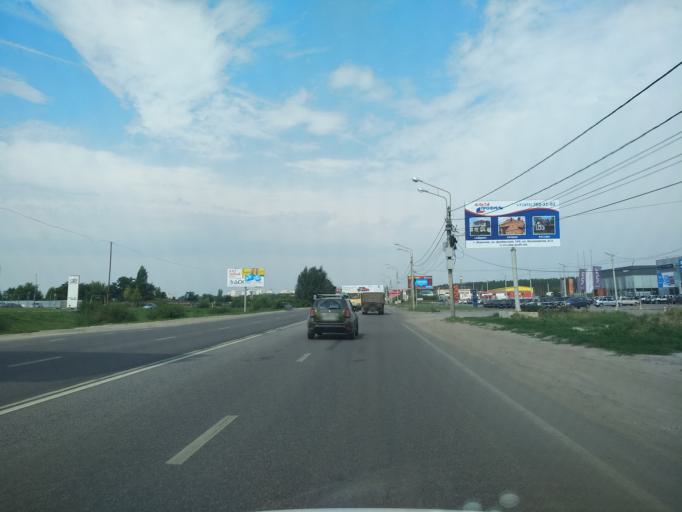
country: RU
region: Voronezj
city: Somovo
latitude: 51.6791
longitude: 39.2907
